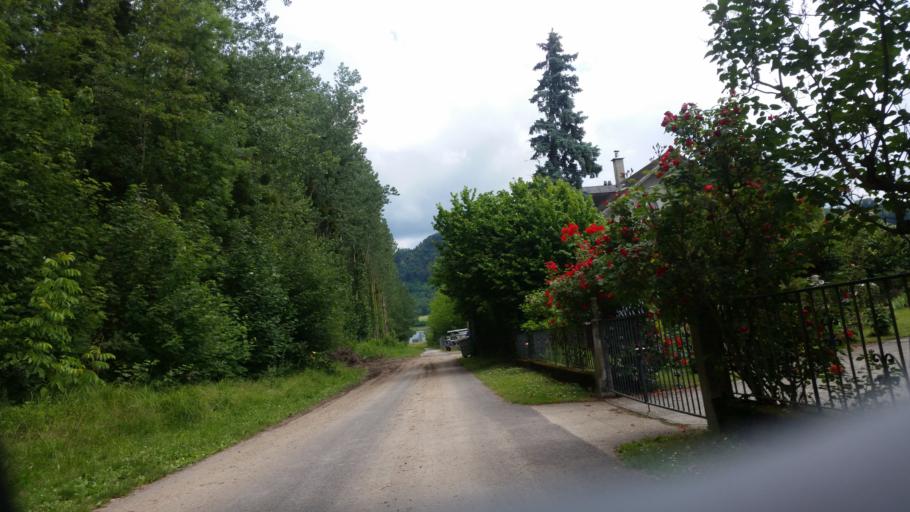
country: CH
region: Vaud
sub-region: Jura-Nord vaudois District
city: Yvonand
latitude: 46.8013
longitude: 6.7478
